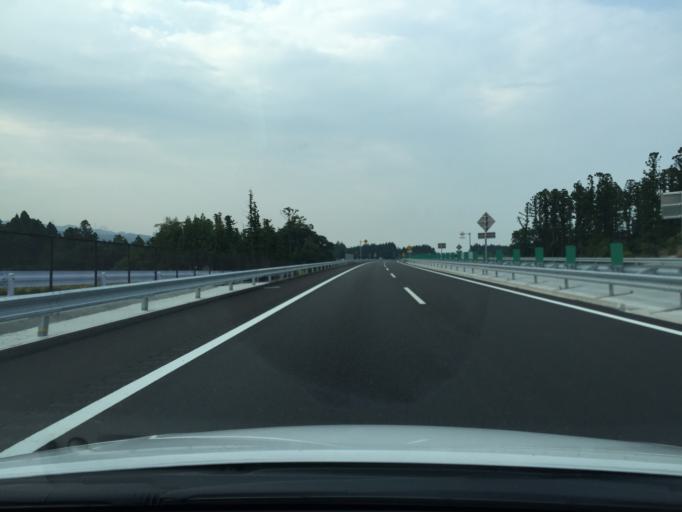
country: JP
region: Fukushima
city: Namie
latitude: 37.5296
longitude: 140.9416
